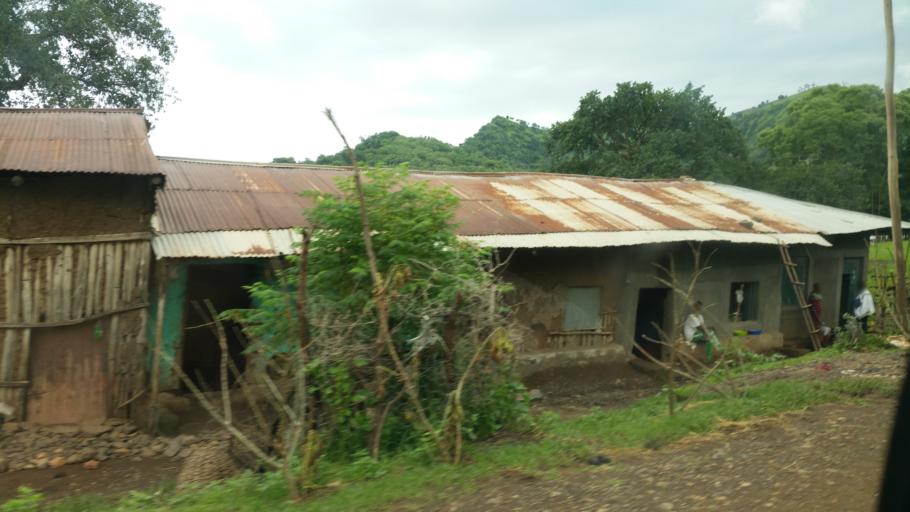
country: ET
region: Amhara
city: Debark'
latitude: 13.3391
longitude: 37.8756
